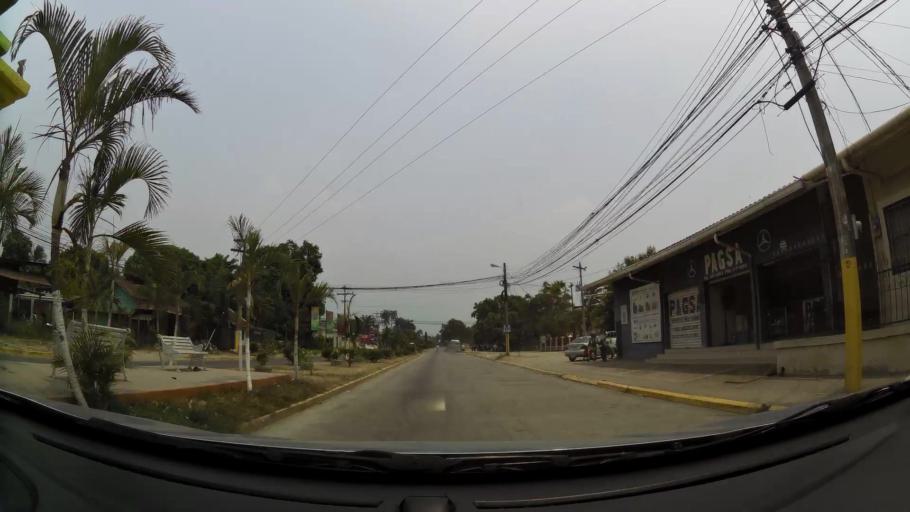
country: HN
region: Yoro
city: El Progreso
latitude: 15.4009
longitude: -87.8137
